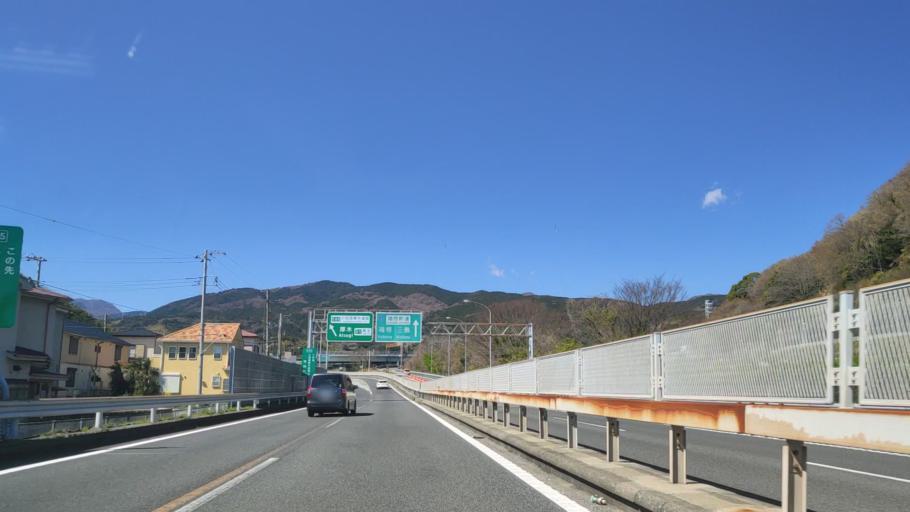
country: JP
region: Kanagawa
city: Odawara
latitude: 35.2457
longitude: 139.1367
